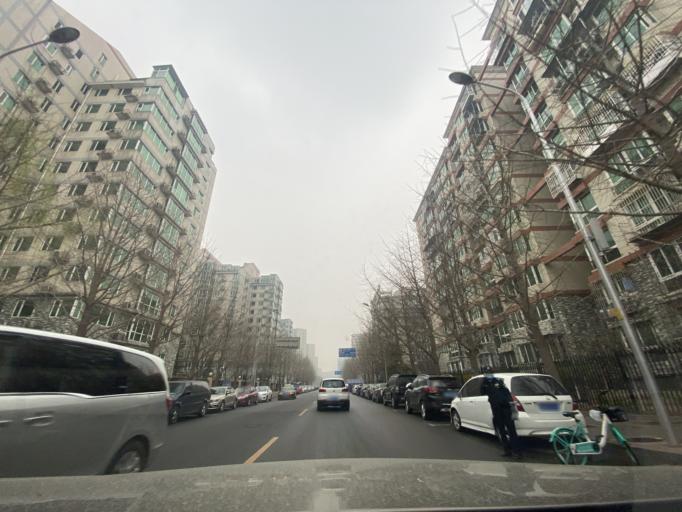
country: CN
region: Beijing
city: Sijiqing
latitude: 39.9624
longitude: 116.2740
